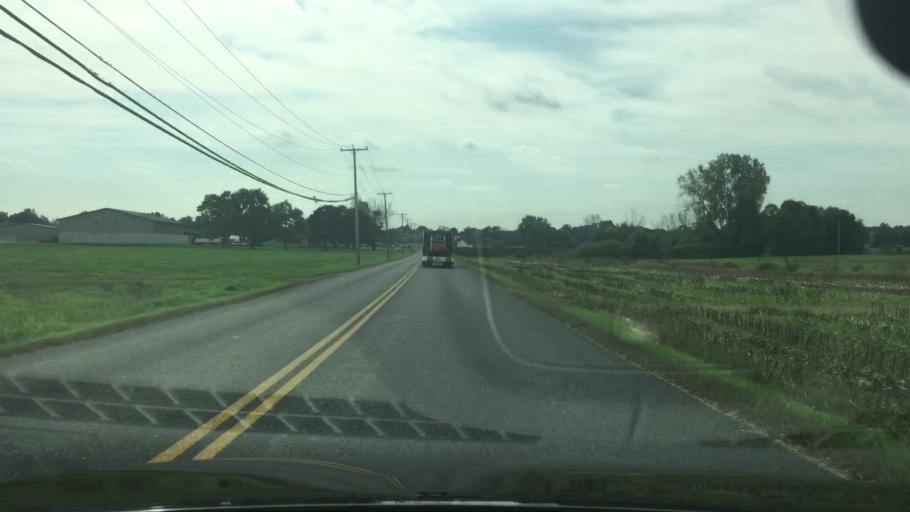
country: US
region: Connecticut
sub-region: Tolland County
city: Ellington
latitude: 41.9137
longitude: -72.4777
